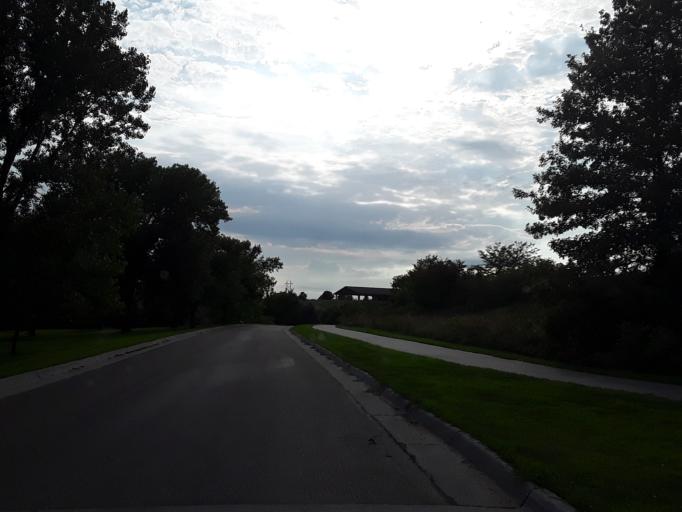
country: US
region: Nebraska
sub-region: Saunders County
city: Ashland
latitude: 41.0231
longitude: -96.3095
